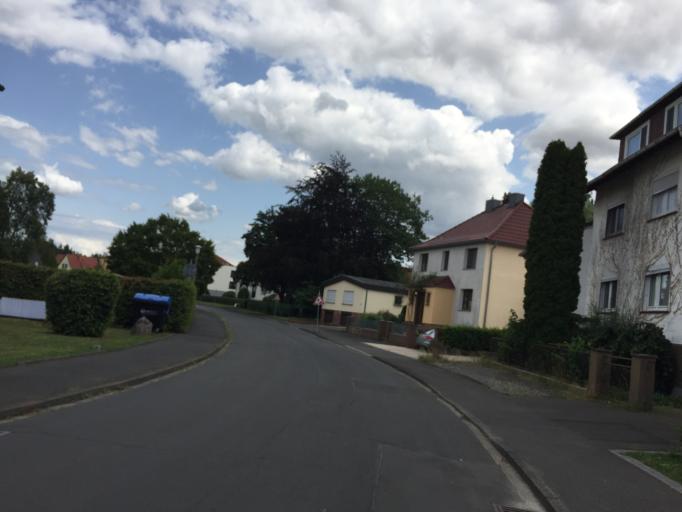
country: DE
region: Hesse
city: Schwalmstadt
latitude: 50.9079
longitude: 9.2363
